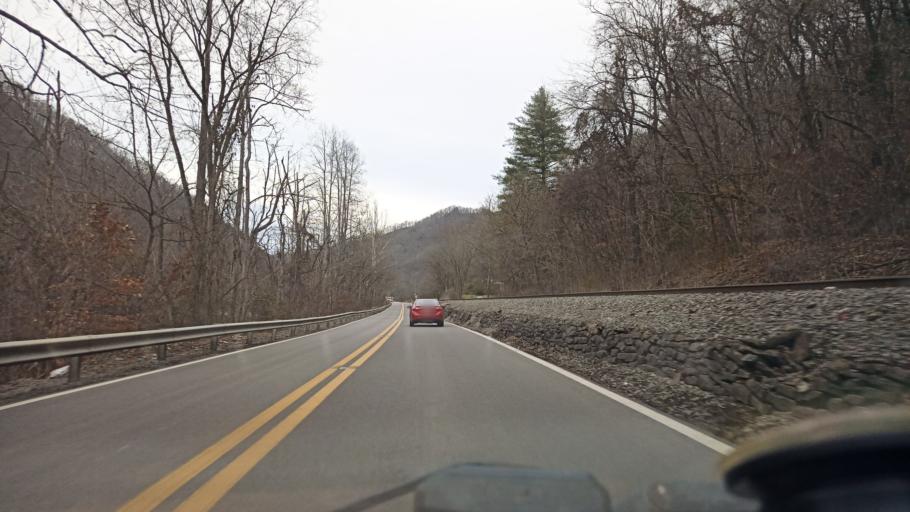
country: US
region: West Virginia
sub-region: Logan County
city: Mallory
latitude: 37.7063
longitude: -81.8665
